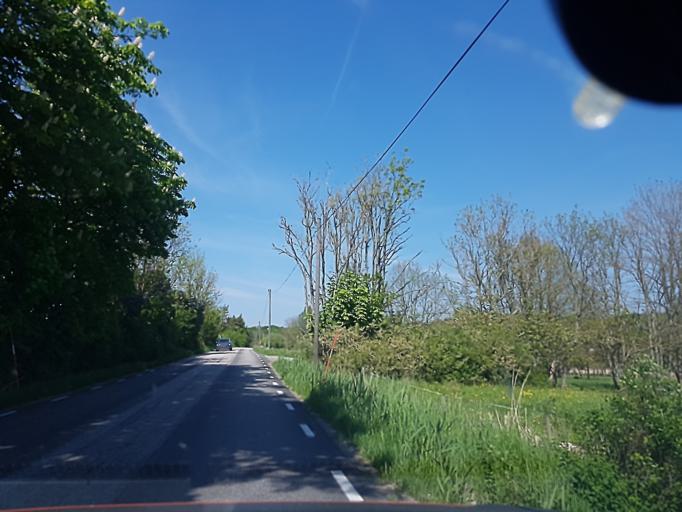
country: SE
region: Vaestra Goetaland
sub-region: Lysekils Kommun
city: Lysekil
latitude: 58.1548
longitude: 11.4612
